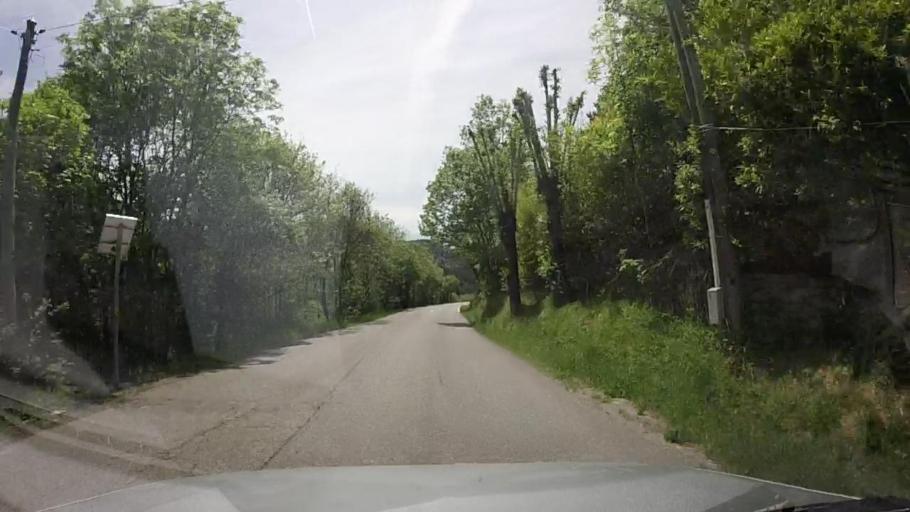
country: FR
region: Provence-Alpes-Cote d'Azur
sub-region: Departement des Alpes-de-Haute-Provence
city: Seyne-les-Alpes
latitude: 44.2743
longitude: 6.3861
